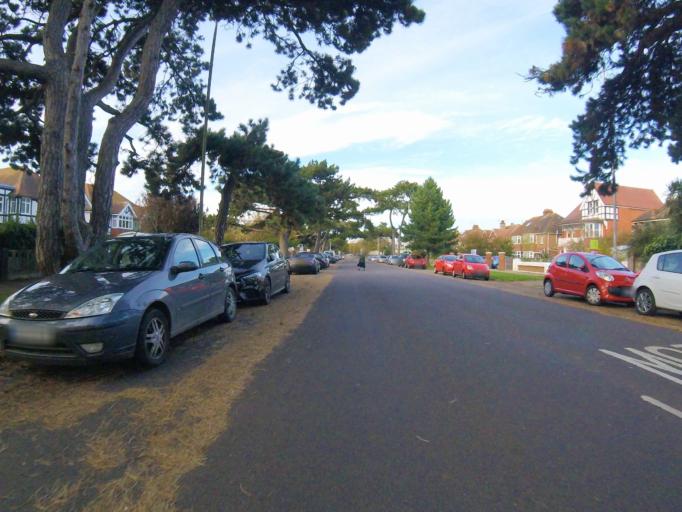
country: GB
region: England
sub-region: West Sussex
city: Worthing
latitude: 50.8169
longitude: -0.3943
